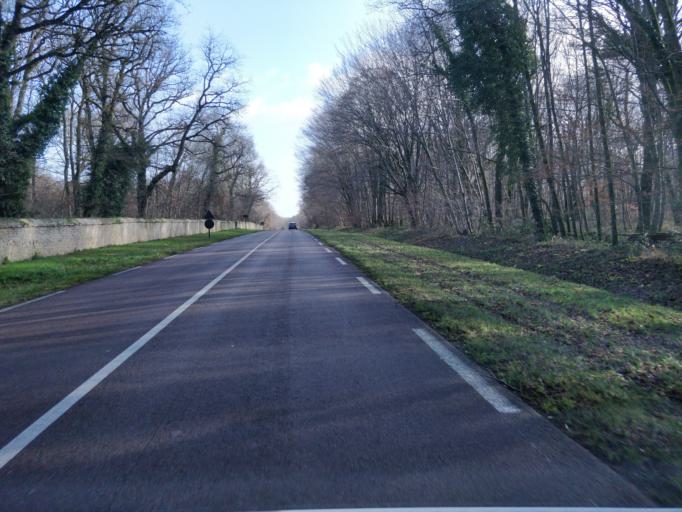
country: FR
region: Ile-de-France
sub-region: Departement de Seine-et-Marne
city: Bagneaux-sur-Loing
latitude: 48.2482
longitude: 2.7719
